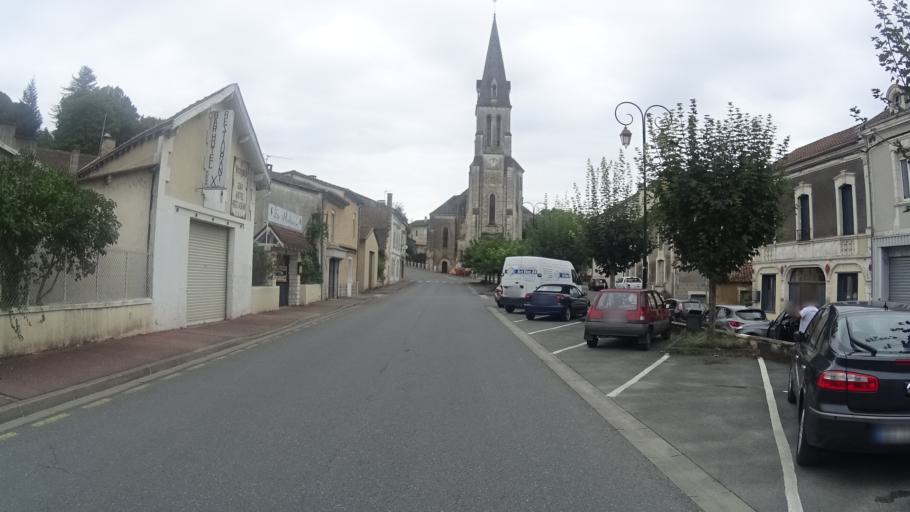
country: FR
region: Aquitaine
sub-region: Departement de la Dordogne
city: Mussidan
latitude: 45.0357
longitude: 0.3690
